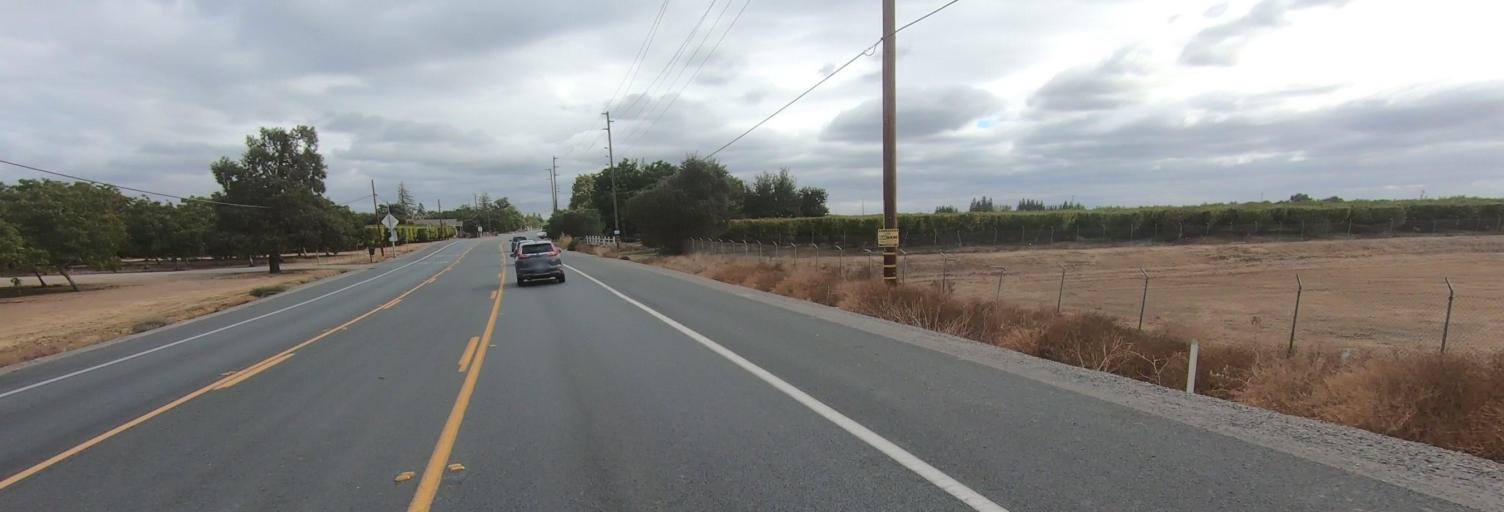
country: US
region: California
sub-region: San Joaquin County
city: Garden Acres
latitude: 37.9746
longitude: -121.2298
